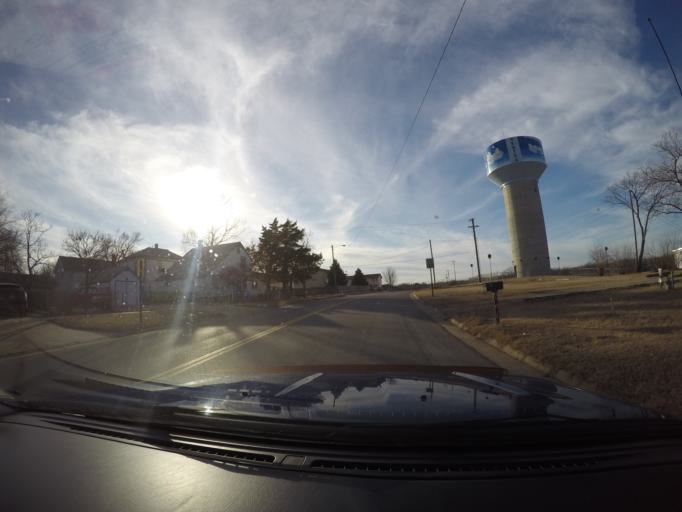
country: US
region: Kansas
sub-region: Harvey County
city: Newton
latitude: 38.0571
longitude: -97.3383
